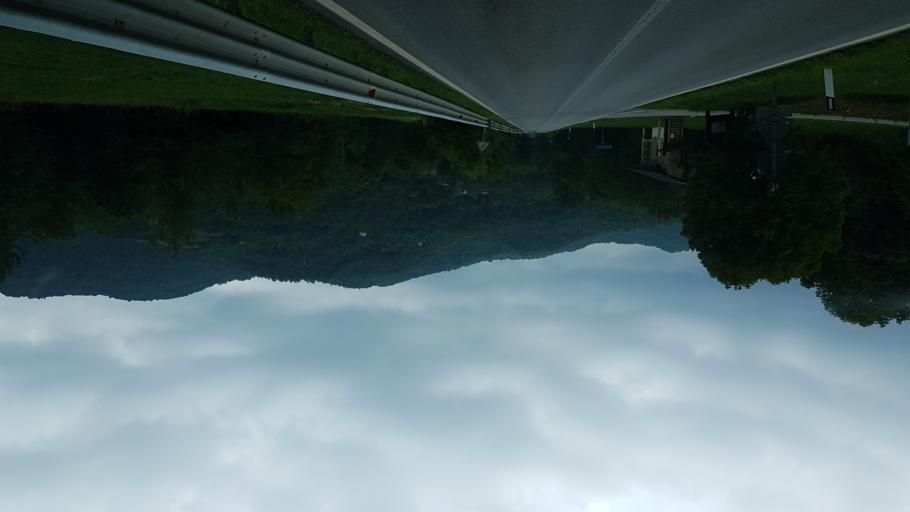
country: IT
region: Piedmont
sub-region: Provincia di Cuneo
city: Moiola
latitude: 44.3275
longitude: 7.3965
